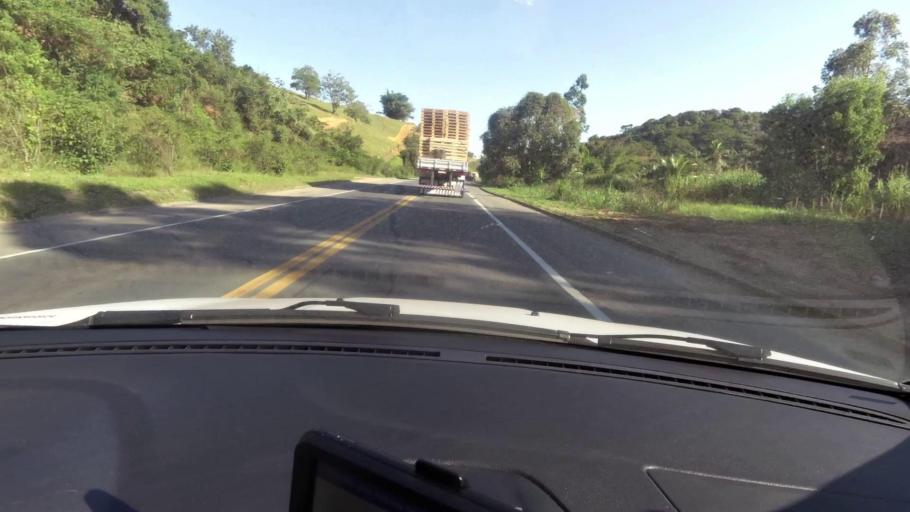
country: BR
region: Espirito Santo
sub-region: Alfredo Chaves
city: Alfredo Chaves
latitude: -20.6704
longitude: -40.6636
